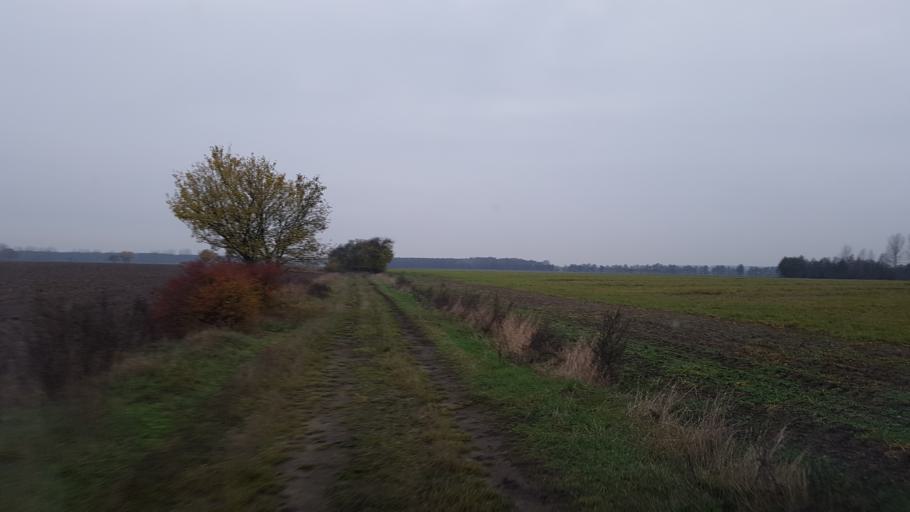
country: DE
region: Brandenburg
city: Schilda
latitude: 51.6204
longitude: 13.3477
